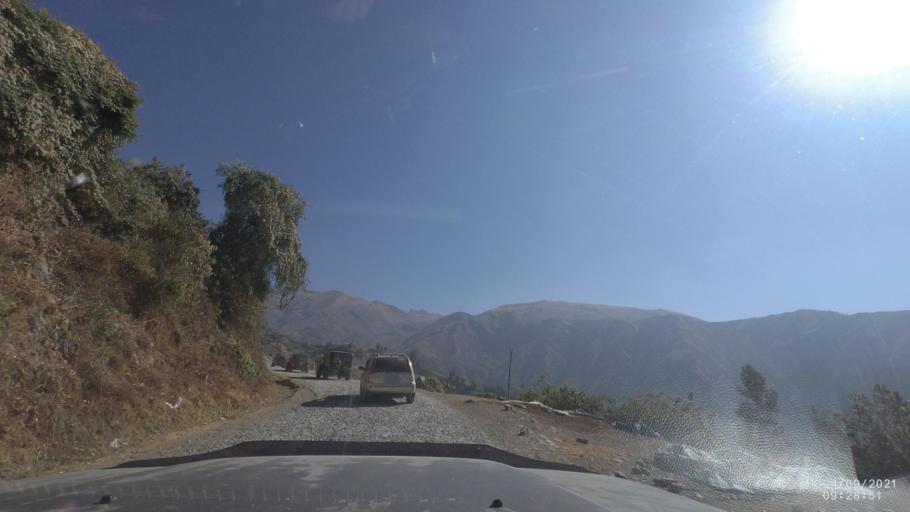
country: BO
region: Cochabamba
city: Sipe Sipe
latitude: -17.3554
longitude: -66.3740
